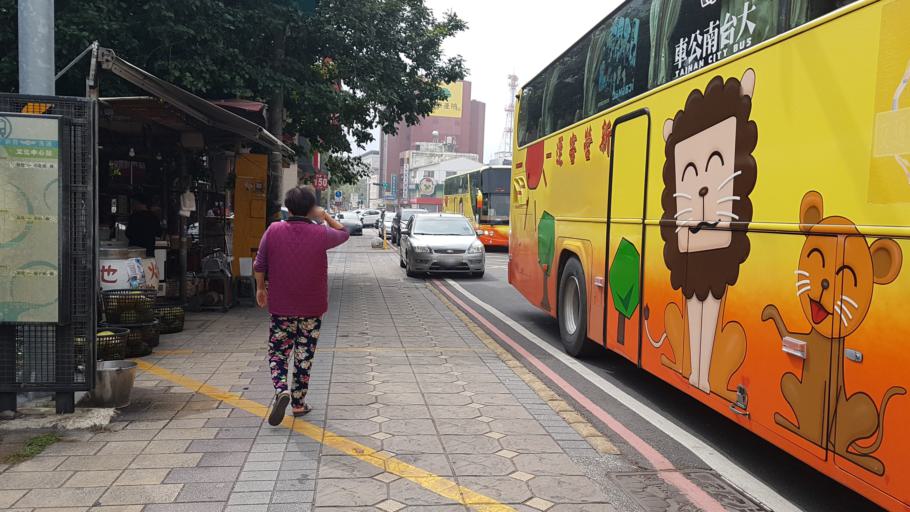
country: TW
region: Taiwan
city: Xinying
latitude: 23.3081
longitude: 120.3161
